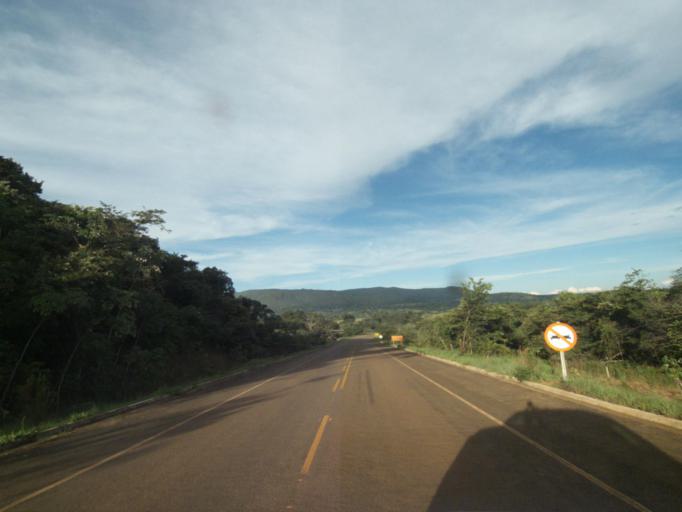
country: BR
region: Goias
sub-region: Jaragua
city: Jaragua
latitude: -15.8452
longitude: -49.3660
